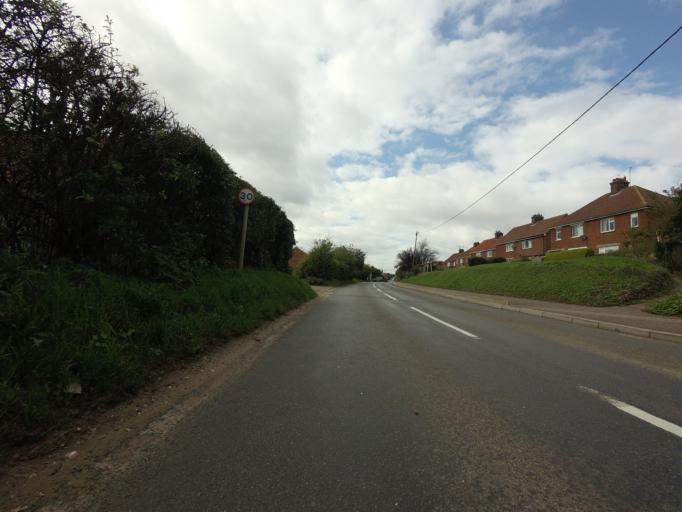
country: GB
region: England
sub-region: Norfolk
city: Snettisham
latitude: 52.8993
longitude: 0.5423
